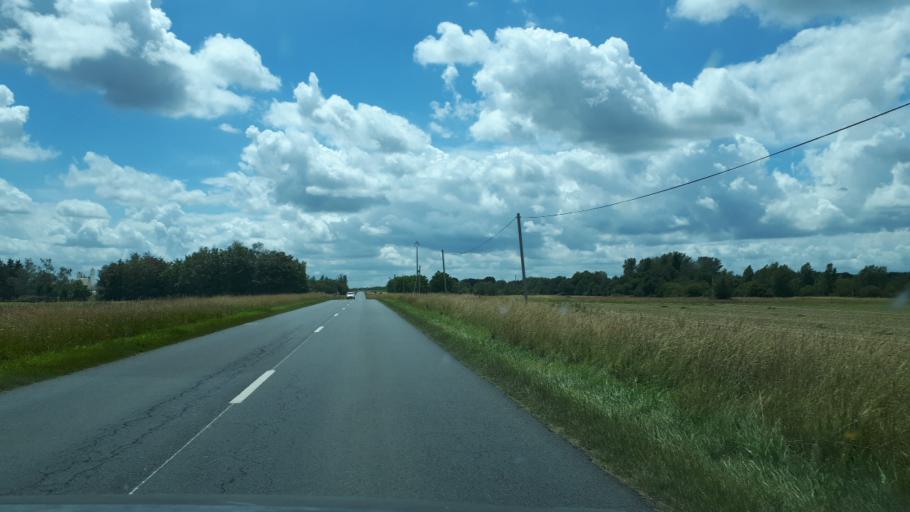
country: FR
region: Centre
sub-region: Departement du Loir-et-Cher
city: Contres
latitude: 47.4022
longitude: 1.4155
